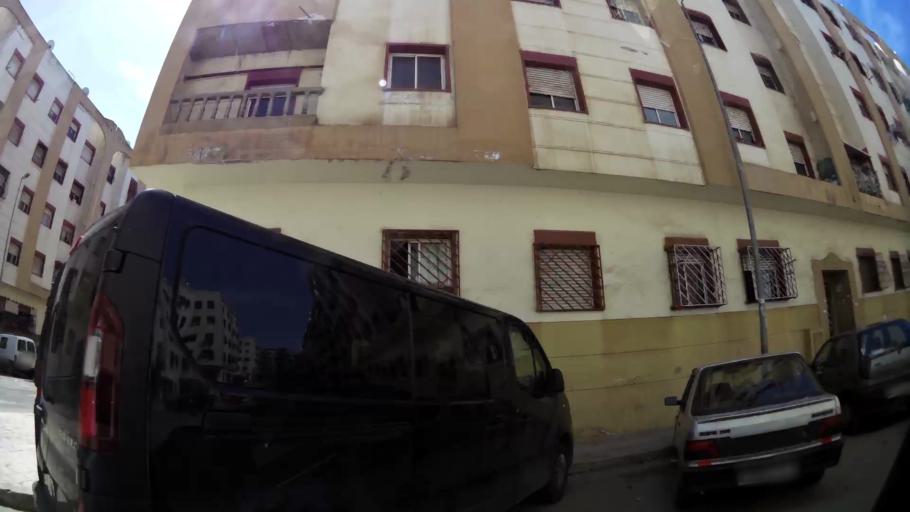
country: MA
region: Grand Casablanca
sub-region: Mediouna
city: Tit Mellil
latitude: 33.5999
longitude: -7.4787
